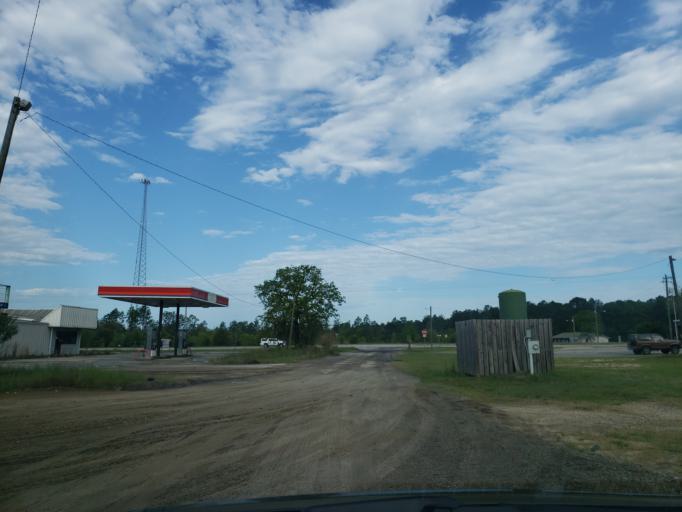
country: US
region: Georgia
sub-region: Emanuel County
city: Swainsboro
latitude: 32.4047
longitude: -82.3040
